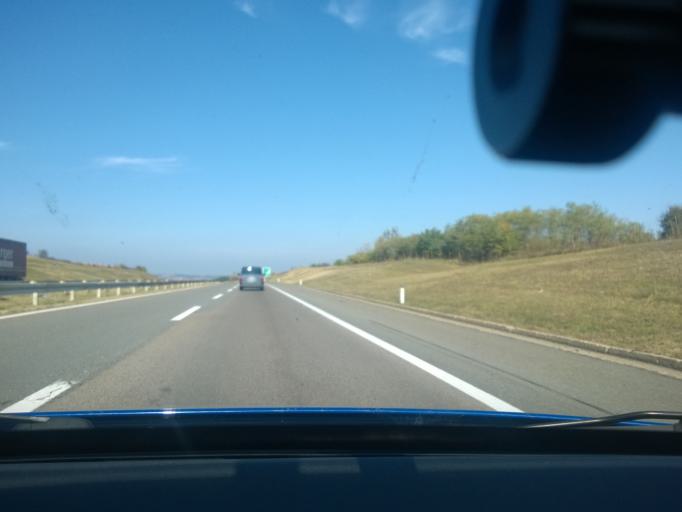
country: RS
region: Central Serbia
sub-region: Nisavski Okrug
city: Razanj
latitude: 43.7100
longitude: 21.5340
